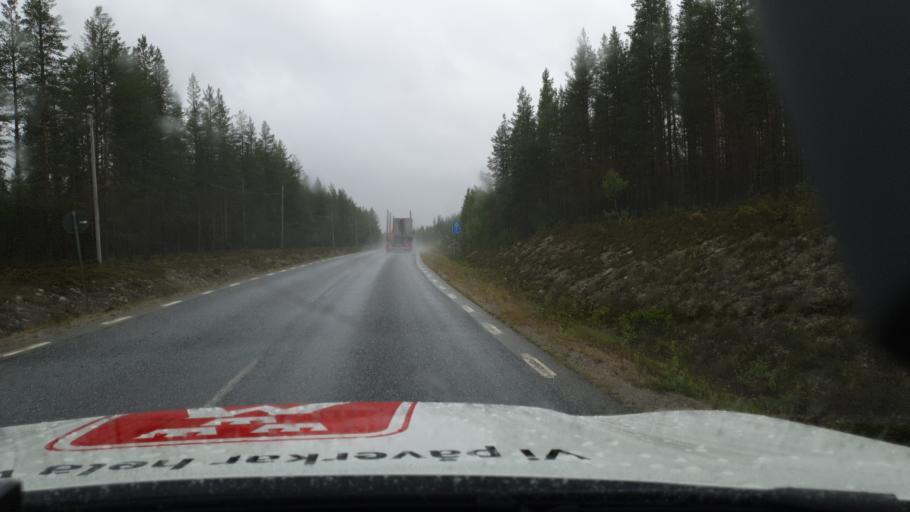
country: SE
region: Vaesterbotten
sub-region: Asele Kommun
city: Asele
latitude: 64.2956
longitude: 17.2583
